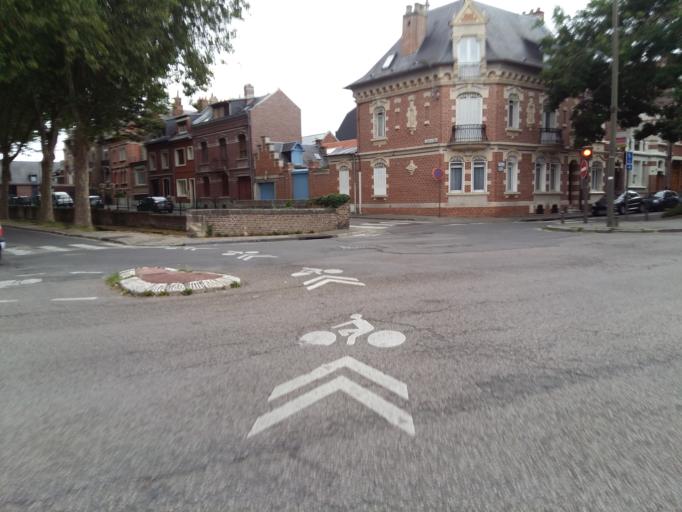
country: FR
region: Picardie
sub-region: Departement de la Somme
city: Amiens
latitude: 49.8969
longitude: 2.2827
